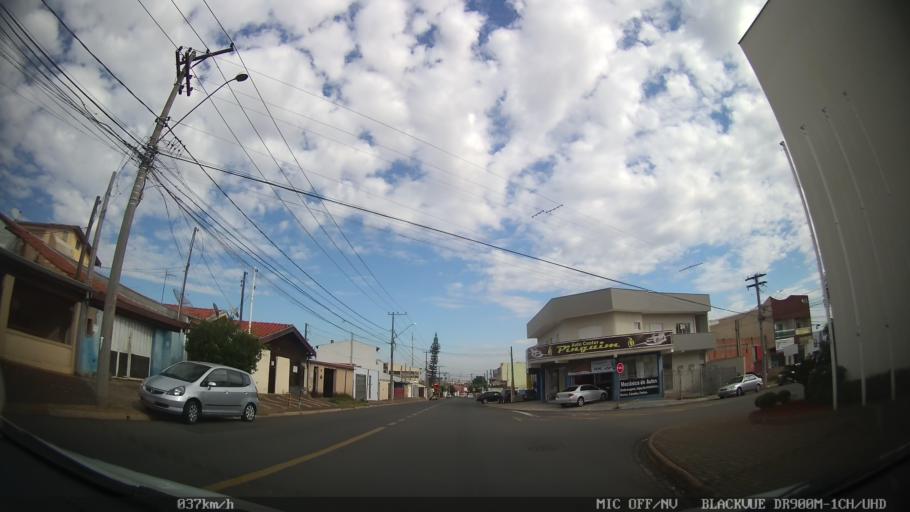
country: BR
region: Sao Paulo
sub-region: Americana
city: Americana
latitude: -22.7390
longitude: -47.3675
